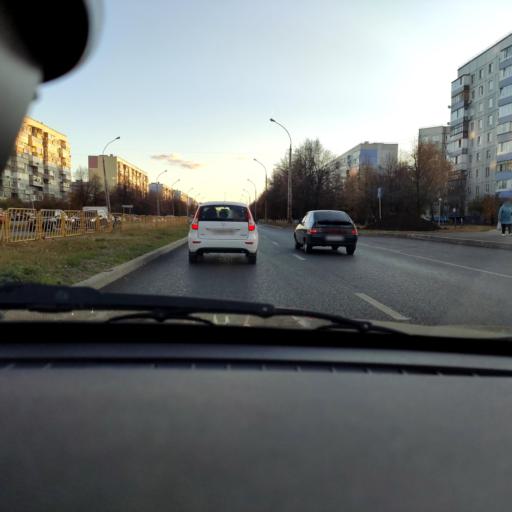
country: RU
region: Samara
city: Tol'yatti
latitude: 53.5414
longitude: 49.3304
